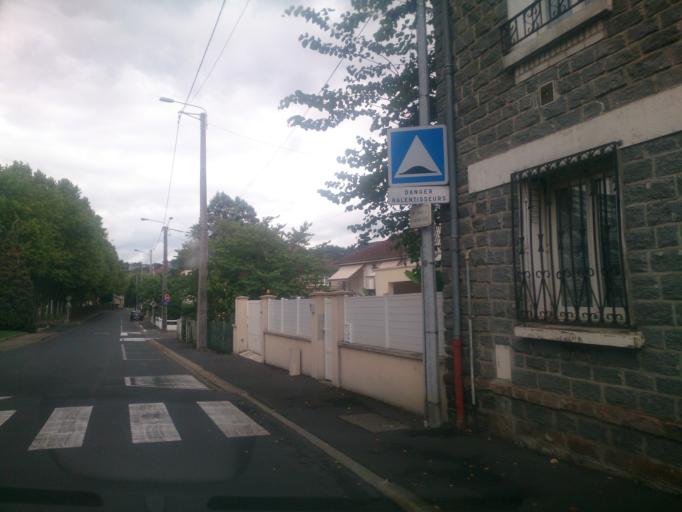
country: FR
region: Limousin
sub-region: Departement de la Correze
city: Malemort-sur-Correze
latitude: 45.1609
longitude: 1.5513
